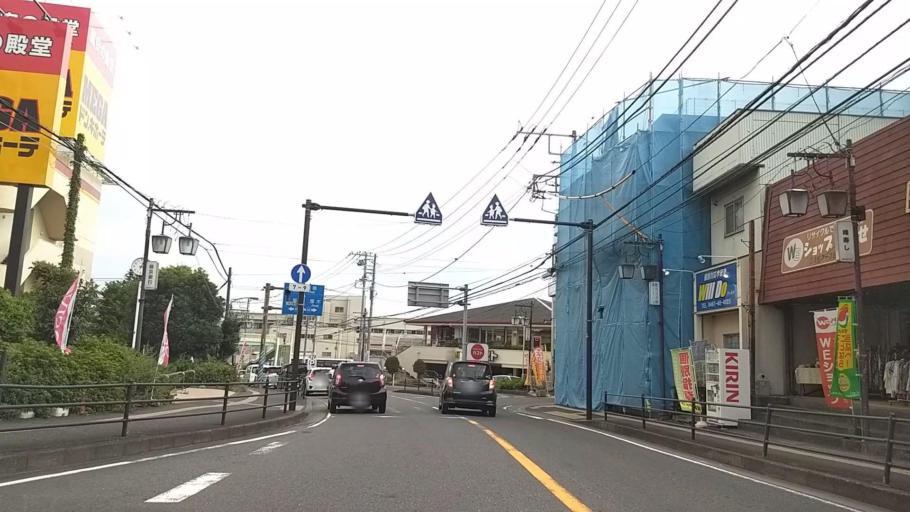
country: JP
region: Kanagawa
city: Minami-rinkan
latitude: 35.4579
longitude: 139.4263
